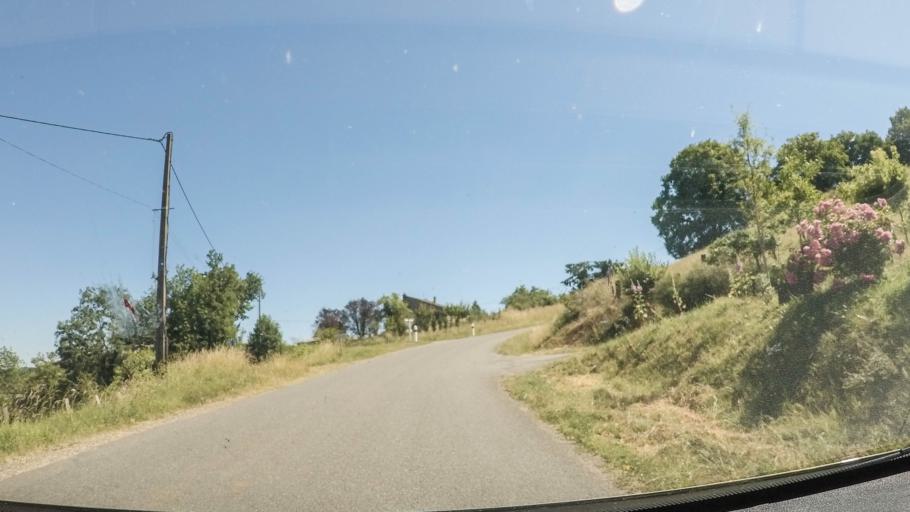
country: FR
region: Midi-Pyrenees
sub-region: Departement de l'Aveyron
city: Firmi
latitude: 44.4771
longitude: 2.3390
